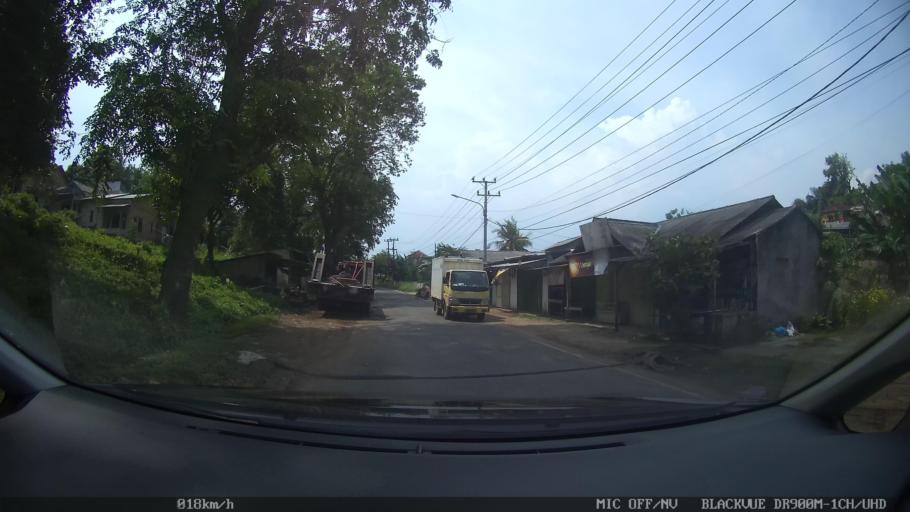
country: ID
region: Lampung
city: Bandarlampung
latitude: -5.4558
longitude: 105.2462
